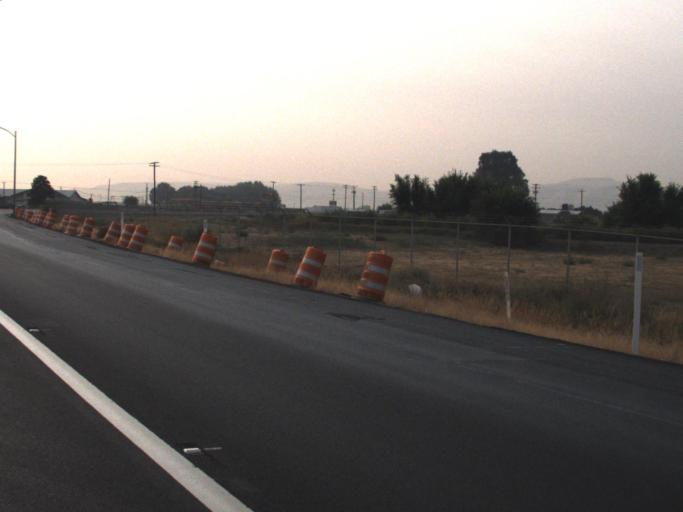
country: US
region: Washington
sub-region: Yakima County
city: Toppenish
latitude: 46.3715
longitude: -120.3227
